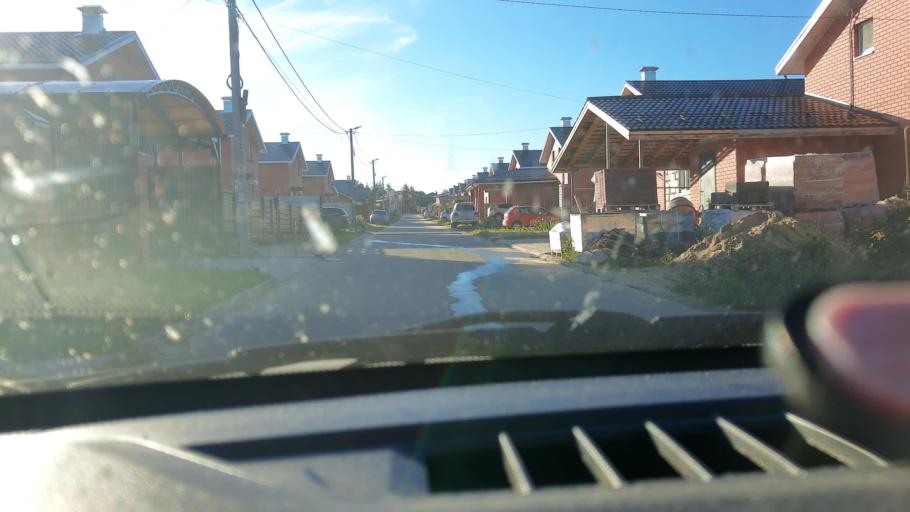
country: RU
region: Nizjnij Novgorod
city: Afonino
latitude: 56.2072
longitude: 44.1383
